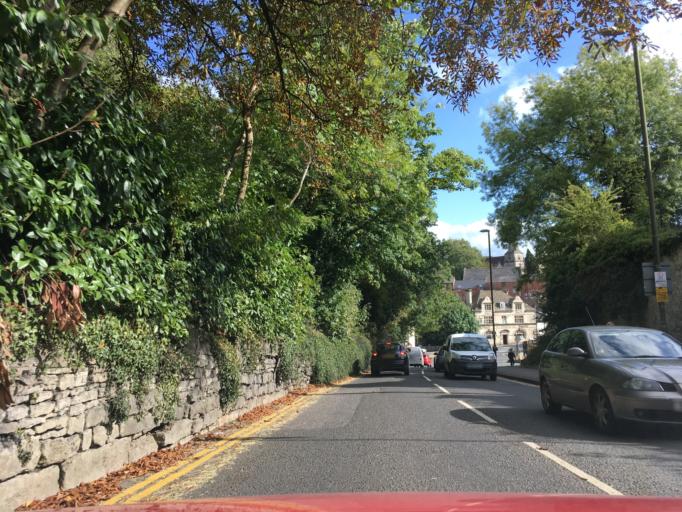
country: GB
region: England
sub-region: Gloucestershire
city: Stroud
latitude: 51.7478
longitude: -2.2185
